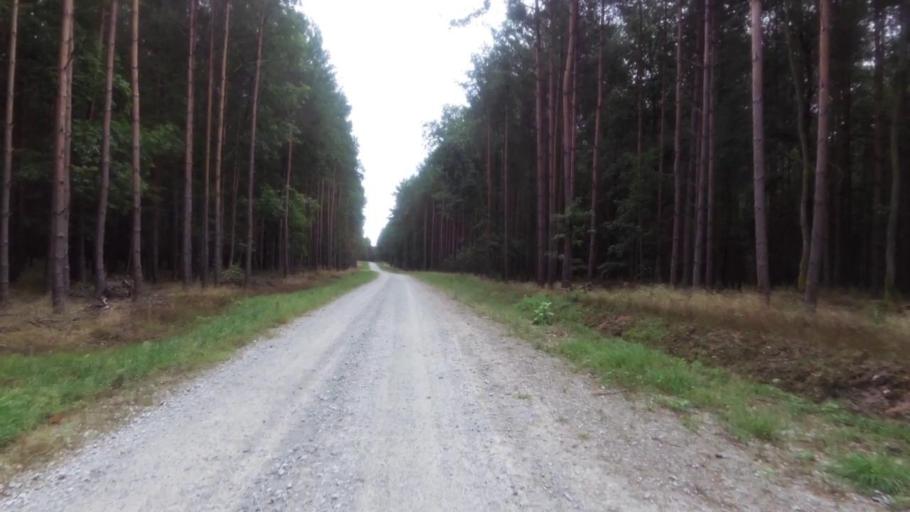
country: PL
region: West Pomeranian Voivodeship
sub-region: Powiat mysliborski
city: Boleszkowice
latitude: 52.6641
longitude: 14.6204
